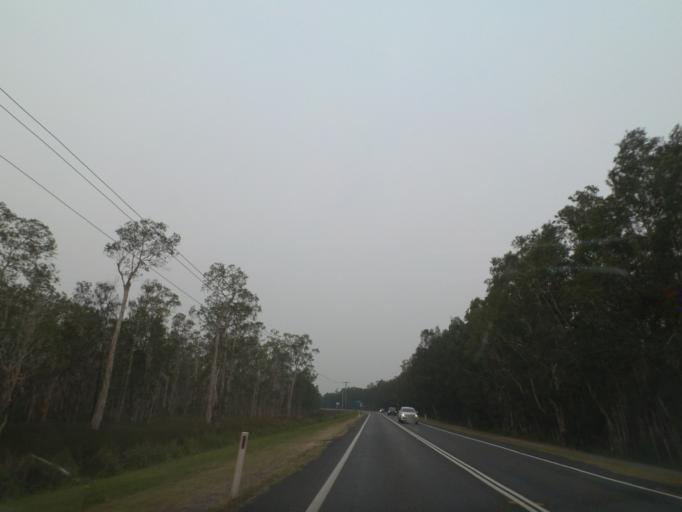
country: AU
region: New South Wales
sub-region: Coffs Harbour
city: Coffs Harbour
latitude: -30.3192
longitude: 153.1076
